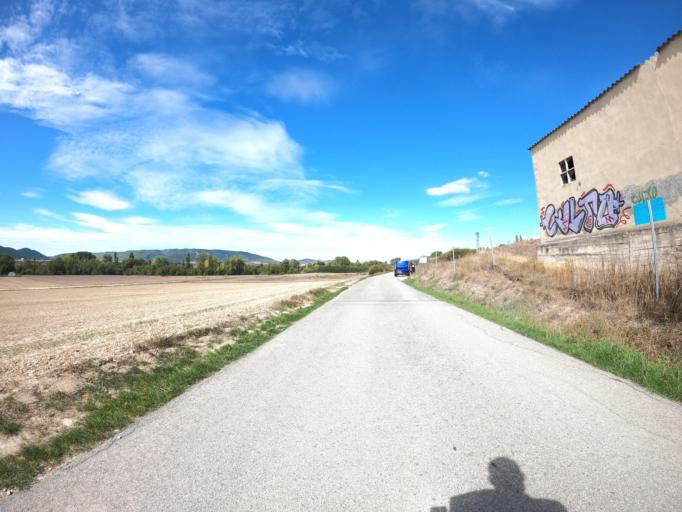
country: ES
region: Navarre
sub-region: Provincia de Navarra
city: Lumbier
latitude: 42.6404
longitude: -1.3098
